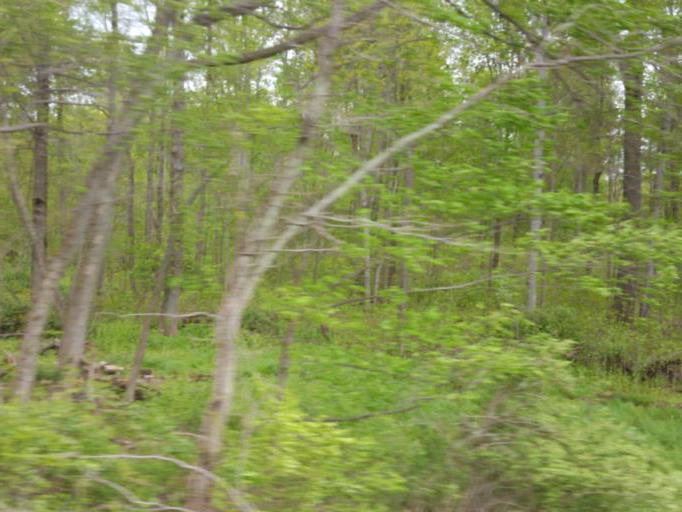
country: US
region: Ohio
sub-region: Knox County
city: Fredericktown
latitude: 40.5574
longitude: -82.5773
